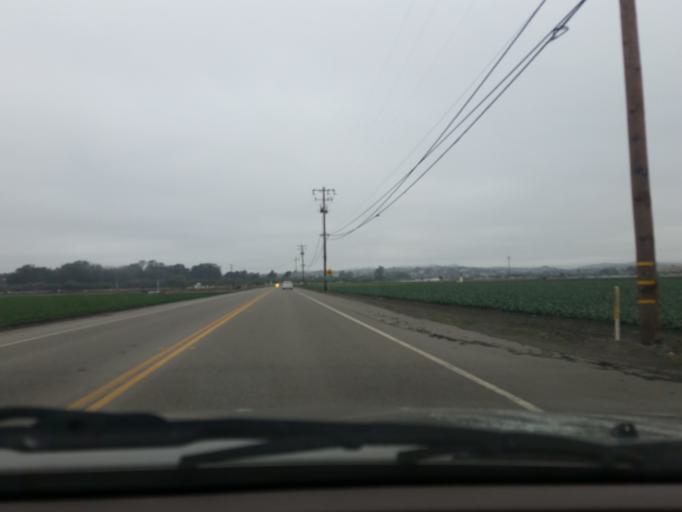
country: US
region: California
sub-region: San Luis Obispo County
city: Oceano
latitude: 35.0883
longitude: -120.5916
